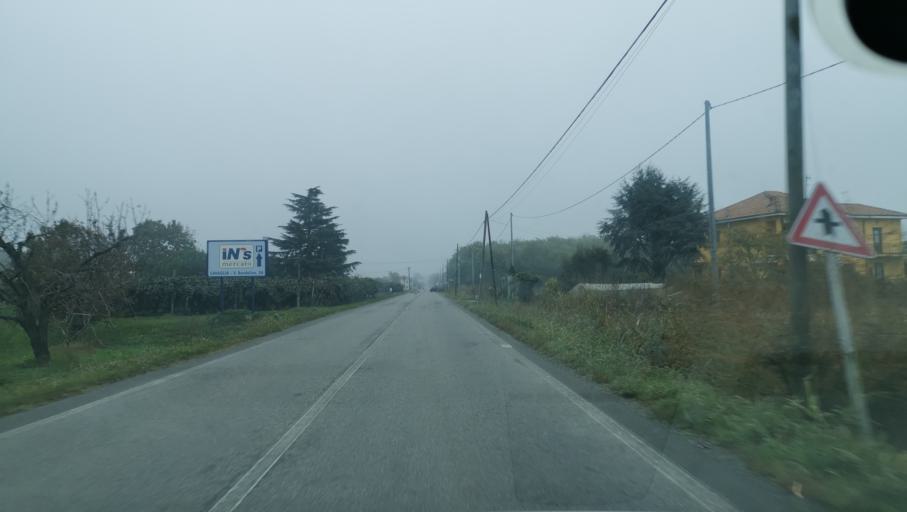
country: IT
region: Piedmont
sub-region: Provincia di Biella
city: Cavaglia
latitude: 45.3926
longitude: 8.0884
